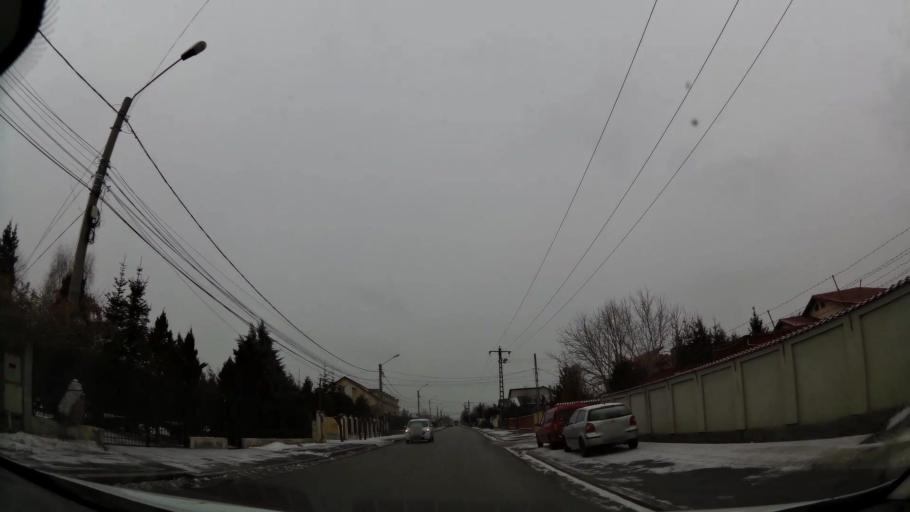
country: RO
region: Dambovita
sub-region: Municipiul Targoviste
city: Targoviste
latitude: 44.9352
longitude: 25.4727
